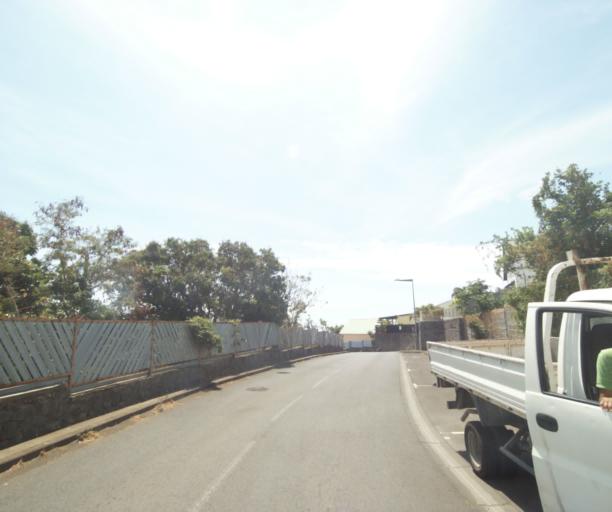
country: RE
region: Reunion
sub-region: Reunion
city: Trois-Bassins
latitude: -21.0990
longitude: 55.2736
